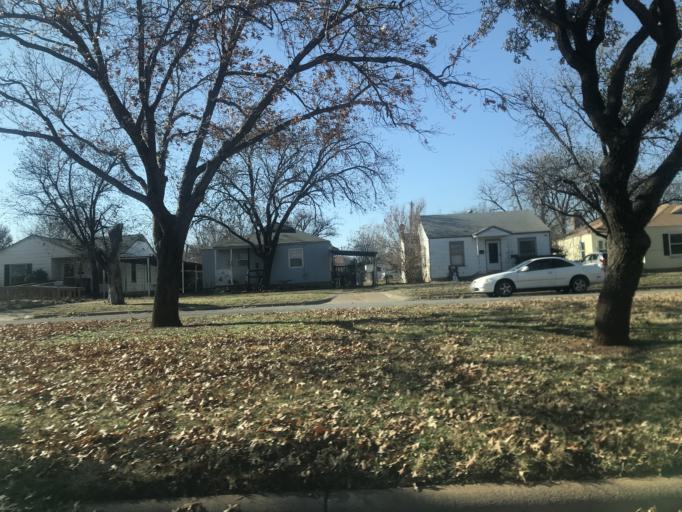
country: US
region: Texas
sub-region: Taylor County
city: Abilene
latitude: 32.4236
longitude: -99.7373
